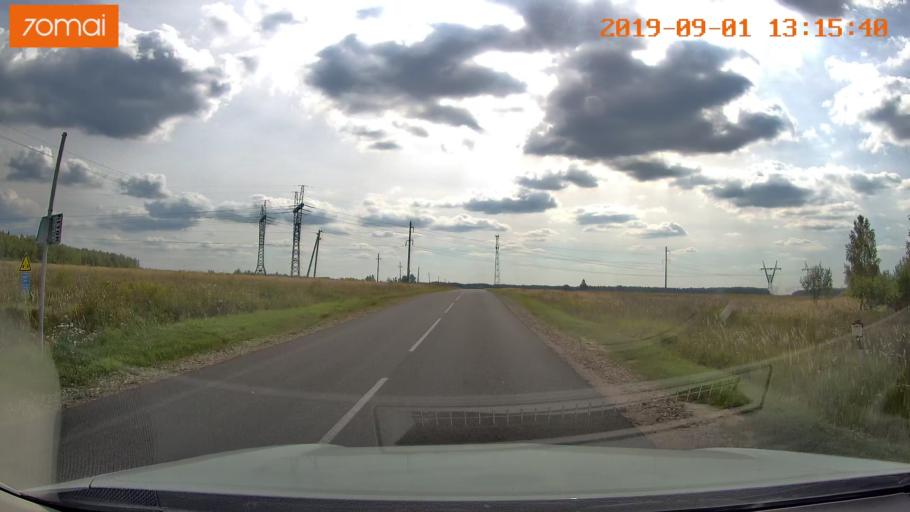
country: RU
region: Kaluga
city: Maloyaroslavets
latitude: 54.9542
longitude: 36.4579
